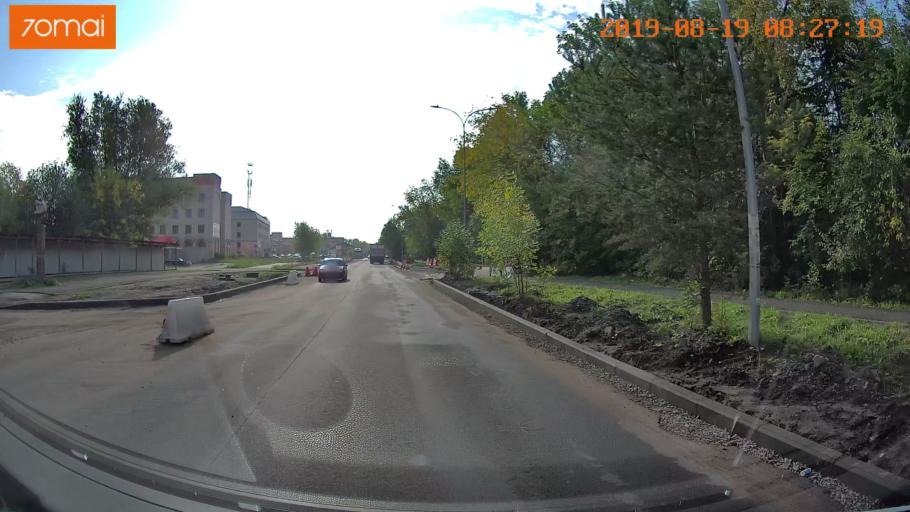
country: RU
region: Ivanovo
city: Bogorodskoye
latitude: 56.9898
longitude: 41.0343
